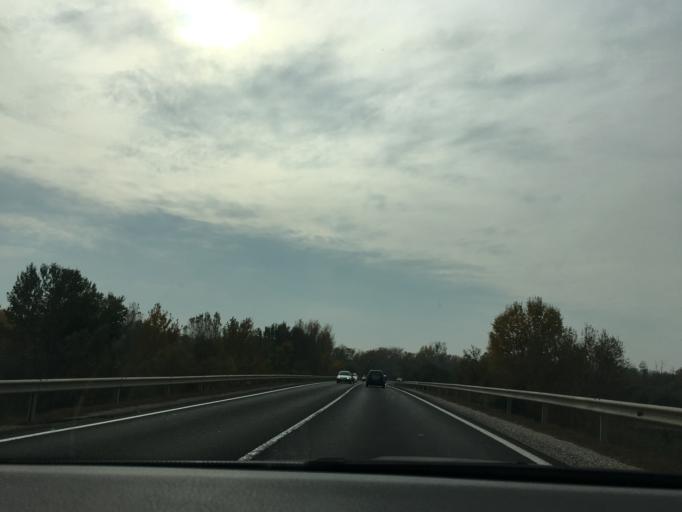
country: HU
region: Hajdu-Bihar
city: Debrecen
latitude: 47.5078
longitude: 21.5942
